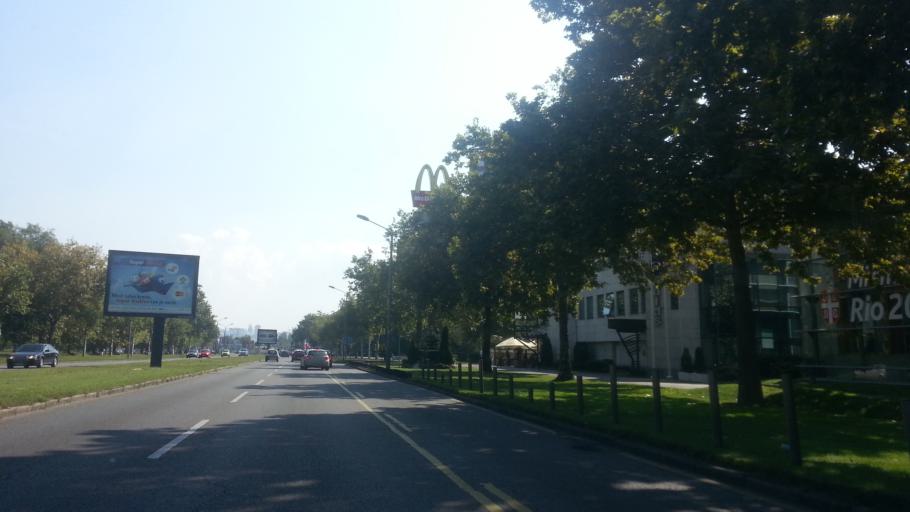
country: RS
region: Central Serbia
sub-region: Belgrade
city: Novi Beograd
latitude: 44.8164
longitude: 20.4304
